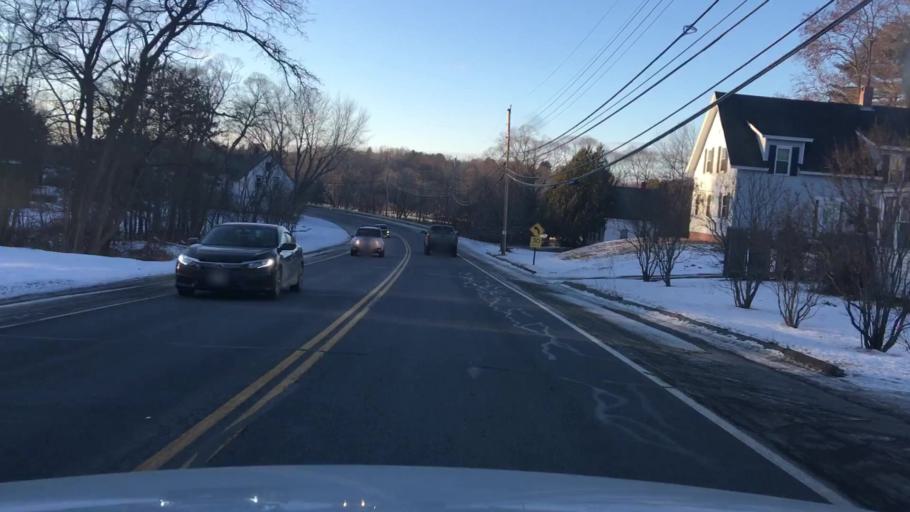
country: US
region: Maine
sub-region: Penobscot County
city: Eddington
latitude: 44.8190
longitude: -68.7115
